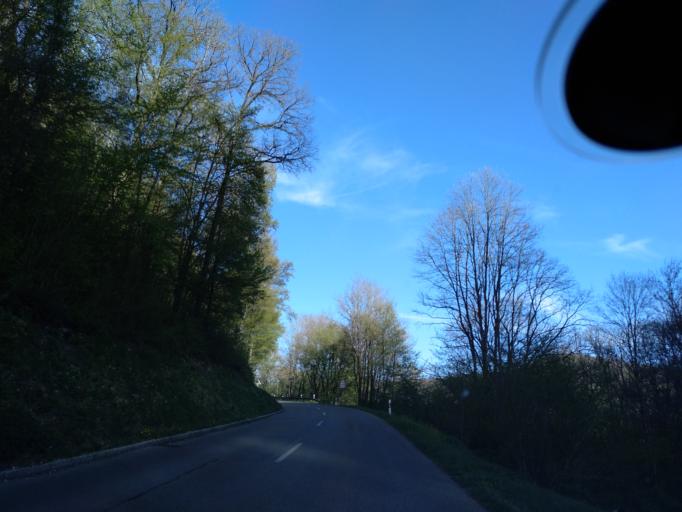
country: DE
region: Baden-Wuerttemberg
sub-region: Regierungsbezirk Stuttgart
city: Langenburg
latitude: 49.2362
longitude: 9.9040
